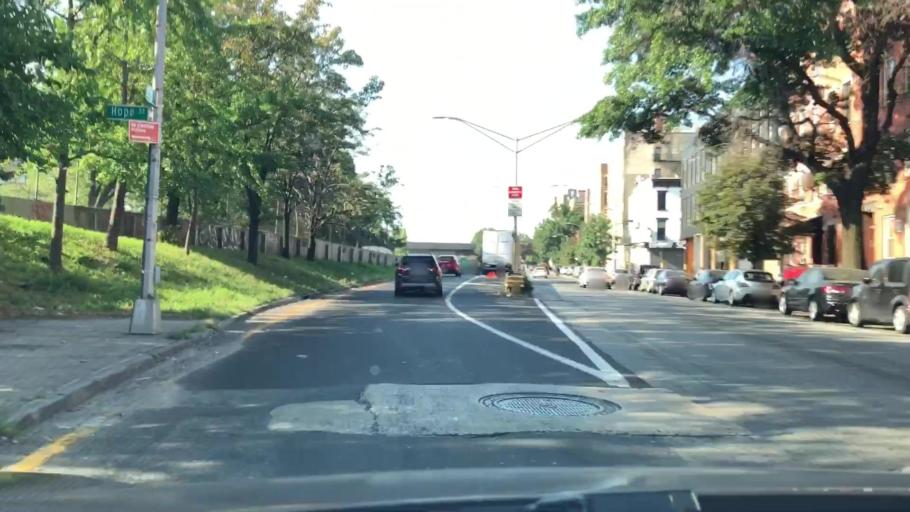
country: US
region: New York
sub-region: Queens County
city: Long Island City
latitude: 40.7130
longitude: -73.9550
